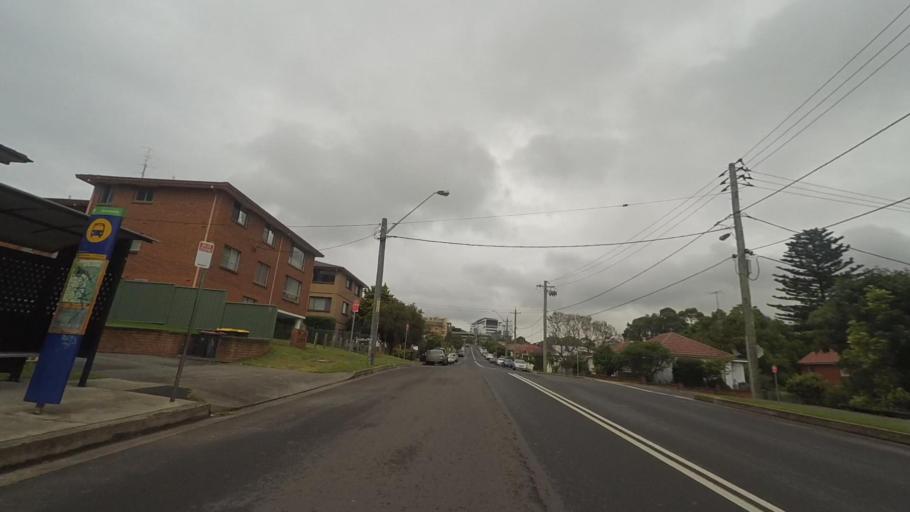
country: AU
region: New South Wales
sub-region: Wollongong
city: Gwynneville
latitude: -34.4210
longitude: 150.8835
